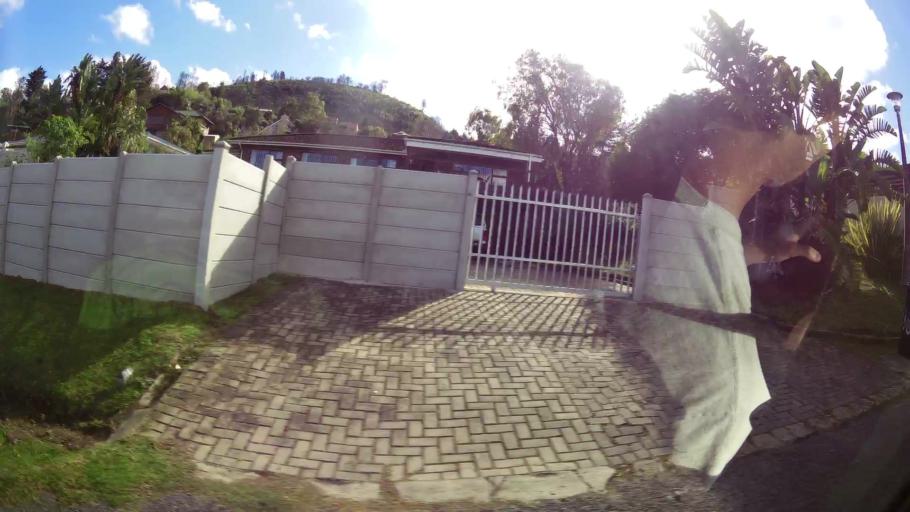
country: ZA
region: Western Cape
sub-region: Eden District Municipality
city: Knysna
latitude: -34.0376
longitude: 23.0695
